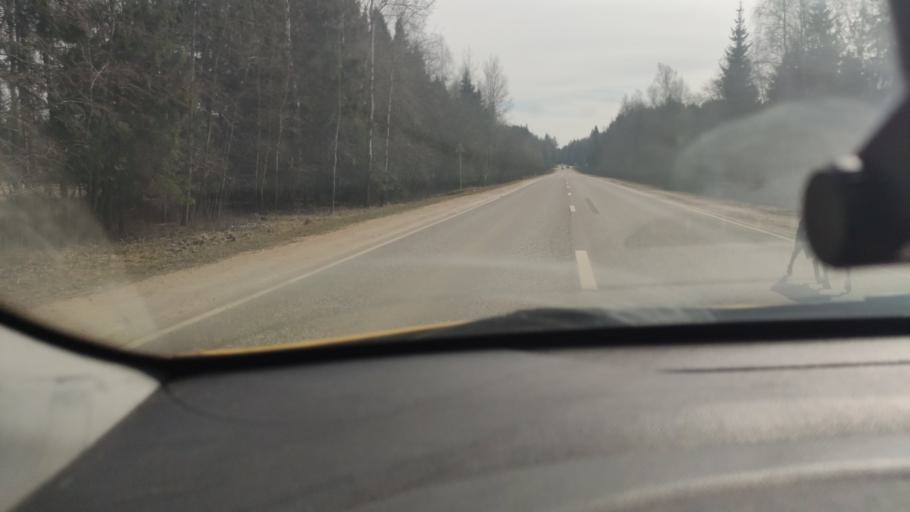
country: RU
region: Moskovskaya
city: Ruza
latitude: 55.7268
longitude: 36.1550
